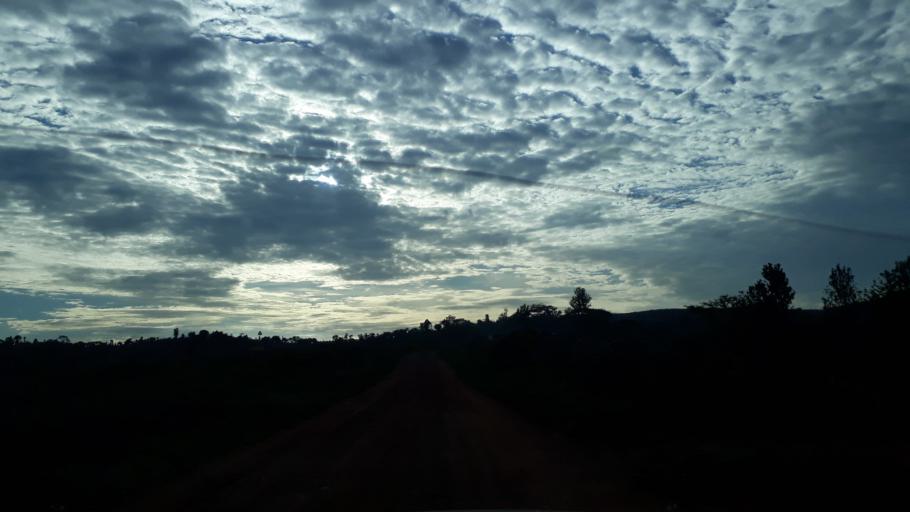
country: UG
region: Northern Region
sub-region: Zombo District
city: Paidha
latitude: 2.2303
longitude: 30.8404
